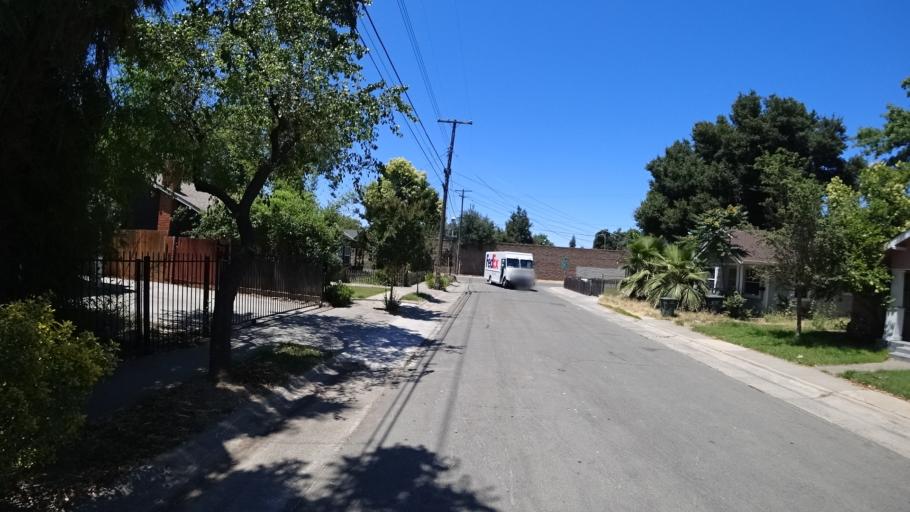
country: US
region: California
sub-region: Sacramento County
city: Sacramento
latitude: 38.5439
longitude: -121.4729
